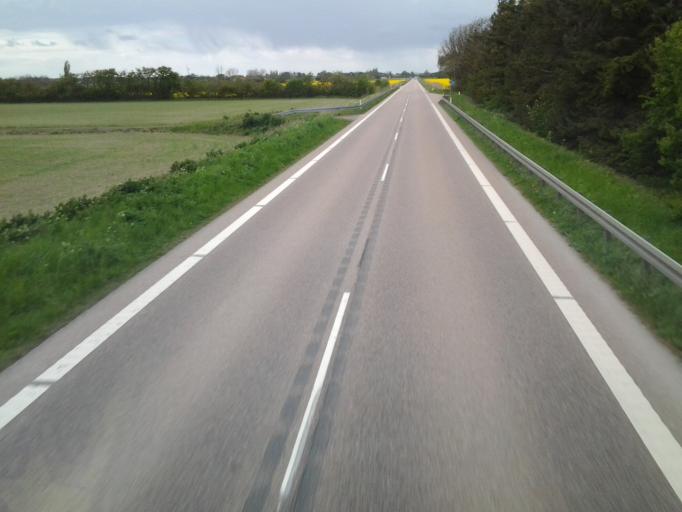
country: DK
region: Zealand
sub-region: Guldborgsund Kommune
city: Nykobing Falster
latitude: 54.6632
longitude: 11.9088
